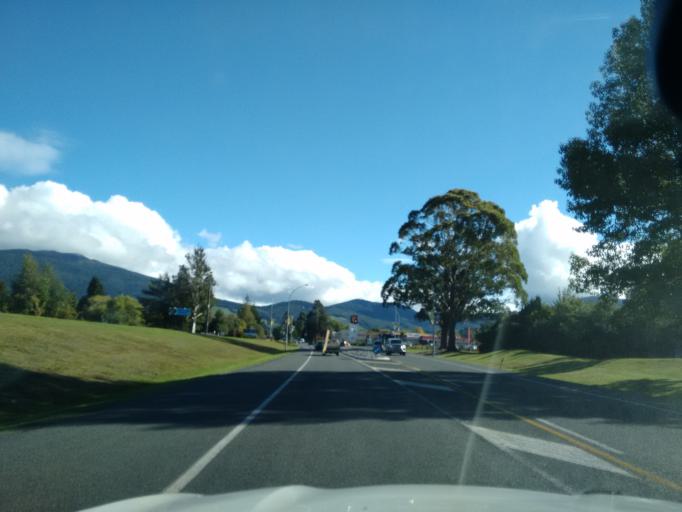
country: NZ
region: Waikato
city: Turangi
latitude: -38.9900
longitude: 175.8125
